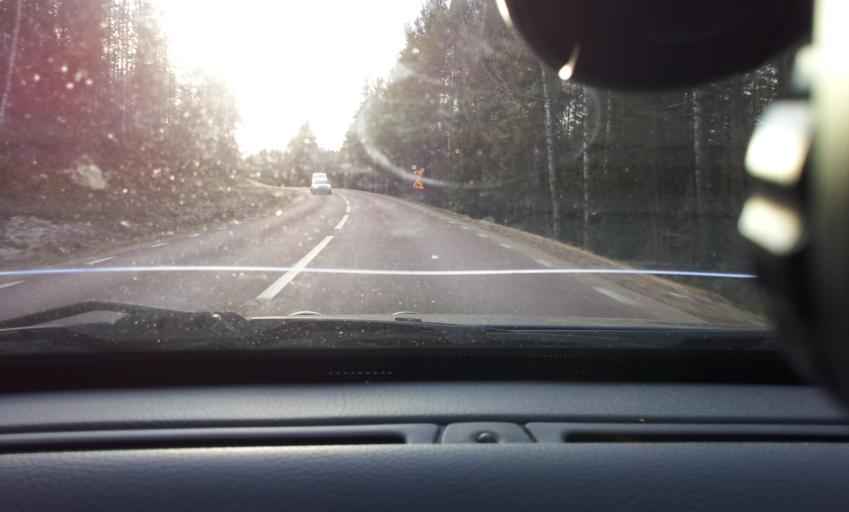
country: SE
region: Jaemtland
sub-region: Harjedalens Kommun
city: Sveg
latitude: 62.1783
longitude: 14.9078
